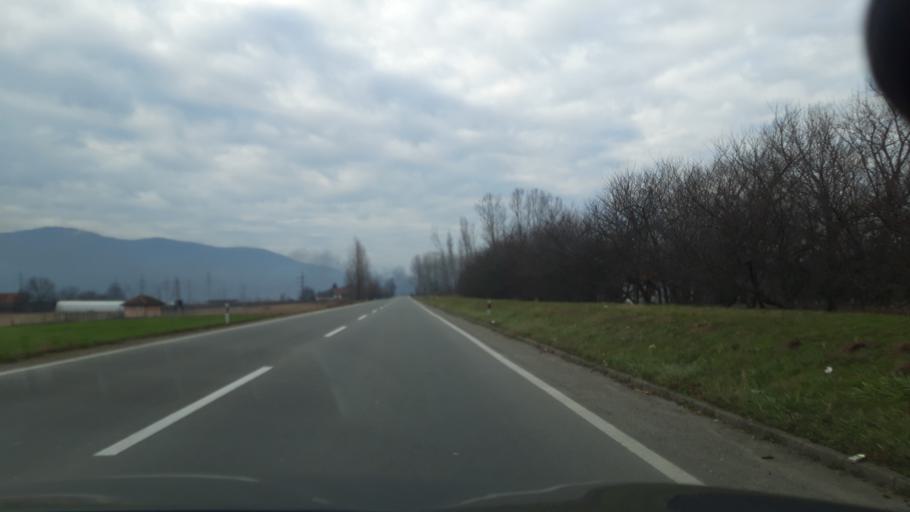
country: RS
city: Lipnicki Sor
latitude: 44.5481
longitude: 19.1946
